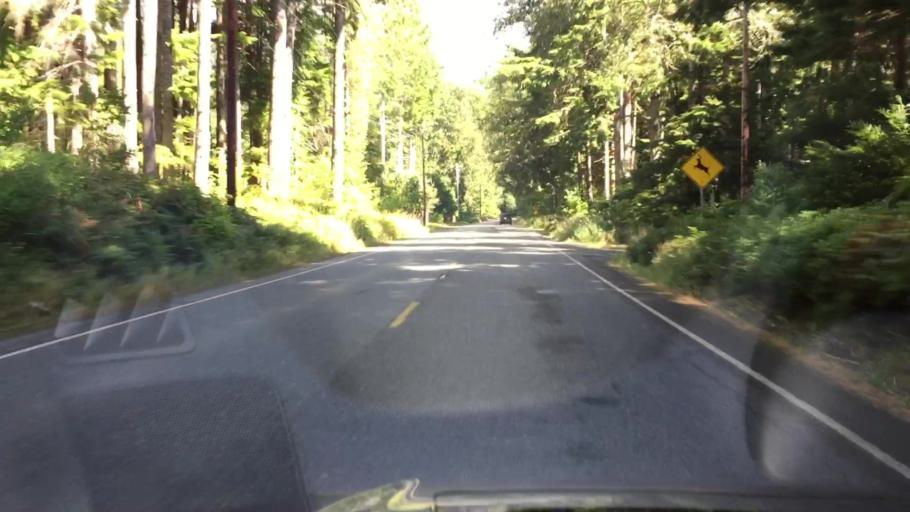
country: US
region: Washington
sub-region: Pierce County
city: Eatonville
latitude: 46.7573
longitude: -121.9800
